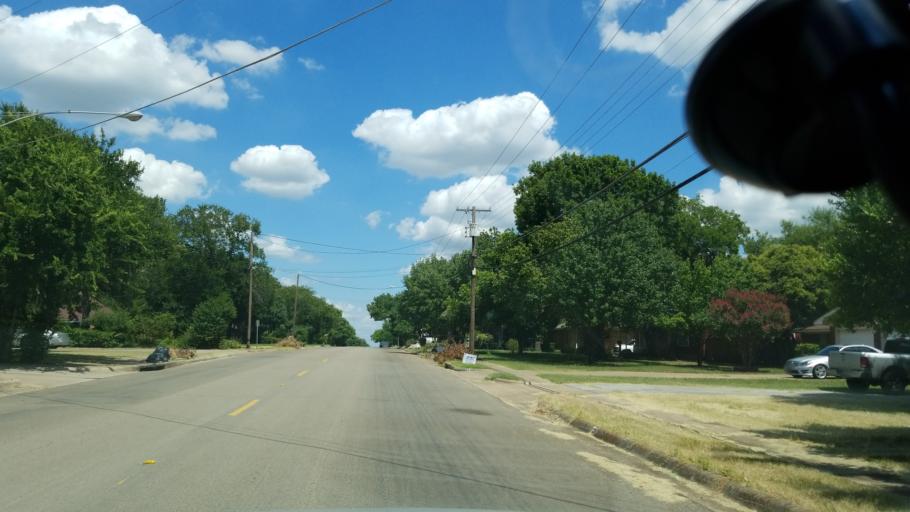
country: US
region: Texas
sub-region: Dallas County
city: Cockrell Hill
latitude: 32.6982
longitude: -96.8725
